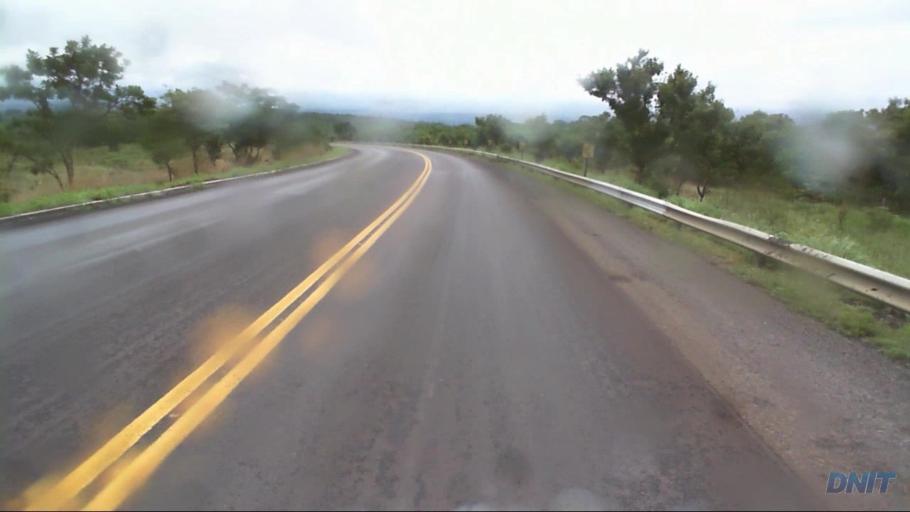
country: BR
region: Goias
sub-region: Padre Bernardo
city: Padre Bernardo
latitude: -15.1947
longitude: -48.4404
